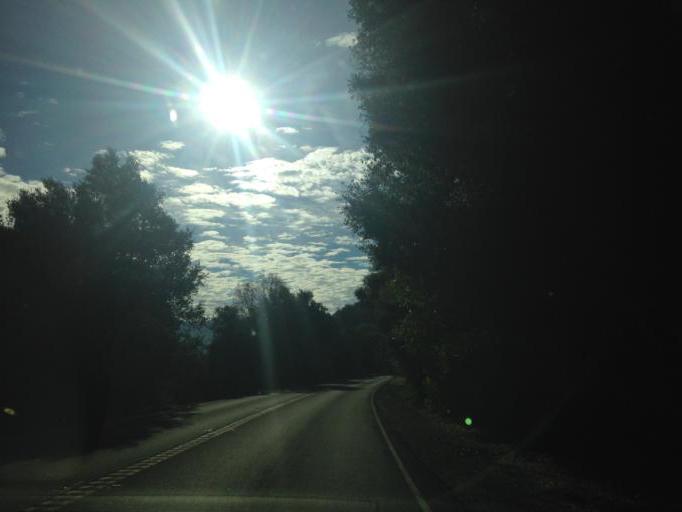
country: US
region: California
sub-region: San Diego County
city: Julian
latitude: 33.2195
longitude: -116.7474
